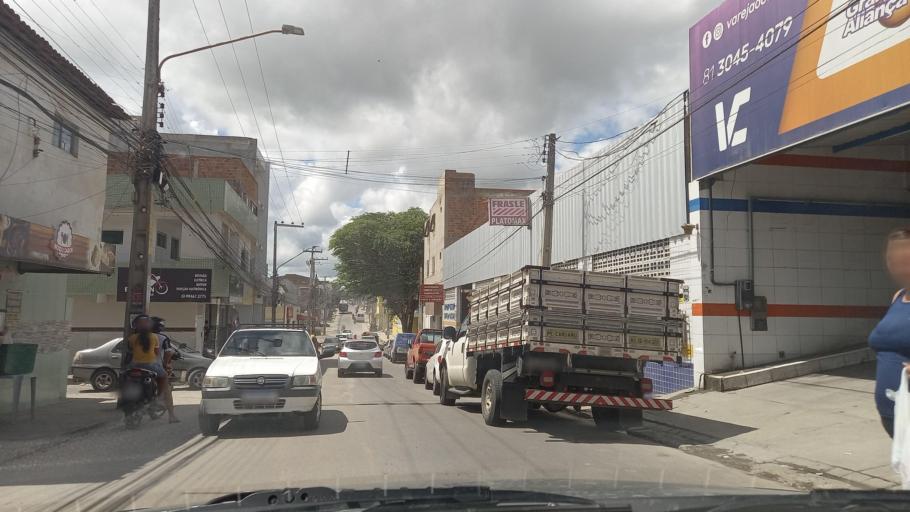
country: BR
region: Pernambuco
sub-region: Caruaru
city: Caruaru
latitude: -8.2824
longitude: -35.9550
